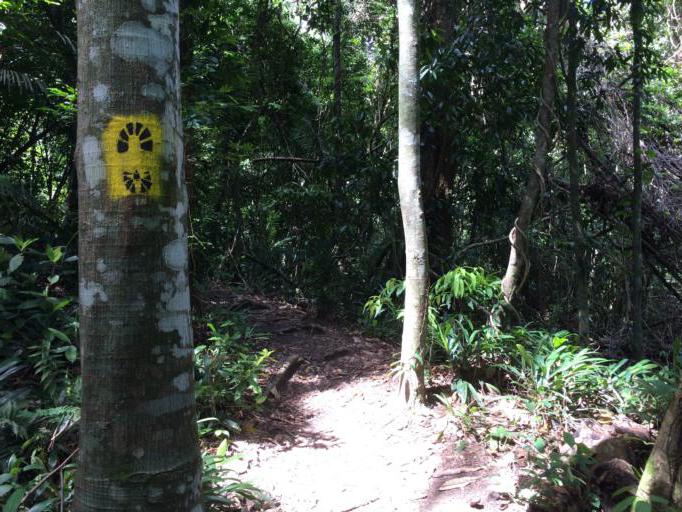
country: BR
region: Rio de Janeiro
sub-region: Rio De Janeiro
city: Rio de Janeiro
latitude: -22.9583
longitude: -43.2106
